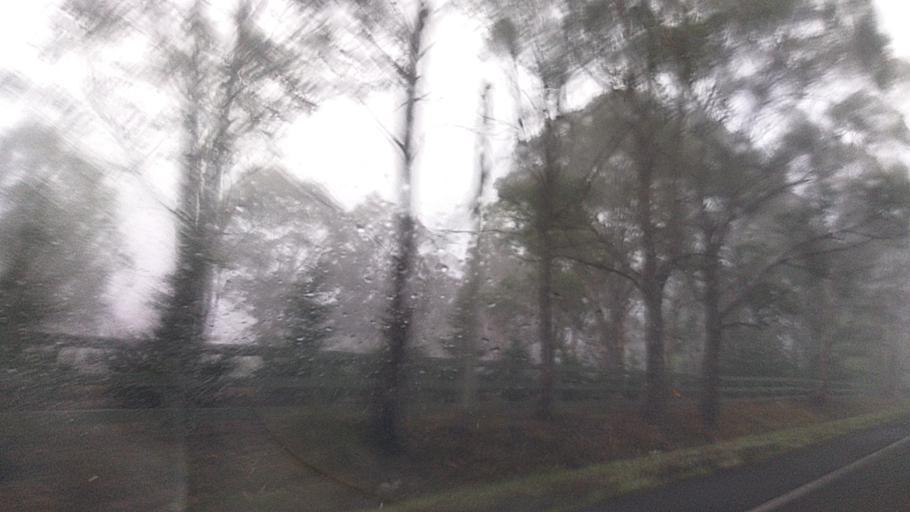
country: AU
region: New South Wales
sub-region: Wollondilly
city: Douglas Park
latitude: -34.2490
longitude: 150.7256
